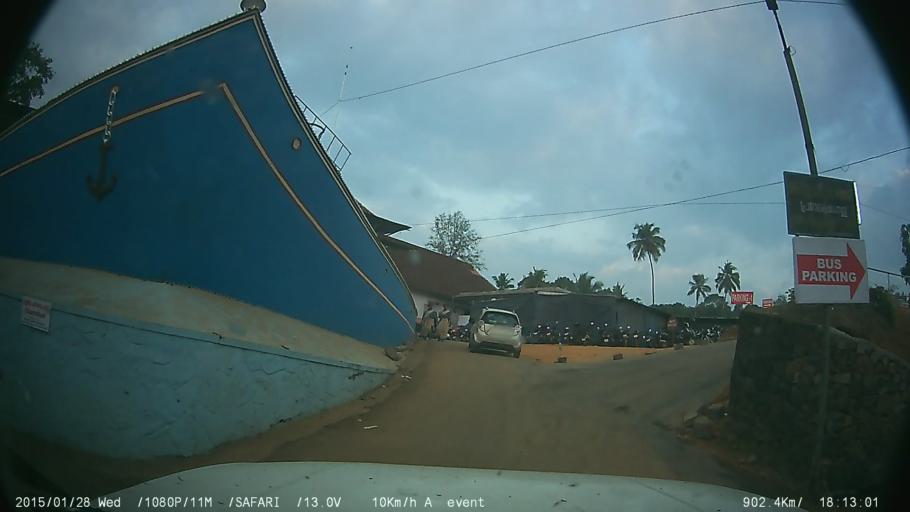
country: IN
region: Kerala
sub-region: Kottayam
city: Palackattumala
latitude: 9.7535
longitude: 76.5648
